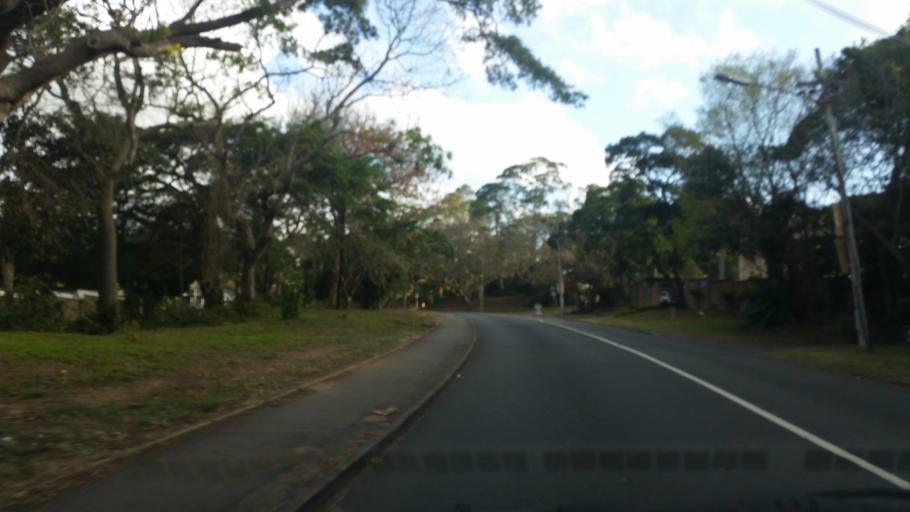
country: ZA
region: KwaZulu-Natal
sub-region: eThekwini Metropolitan Municipality
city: Berea
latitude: -29.8296
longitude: 30.9224
